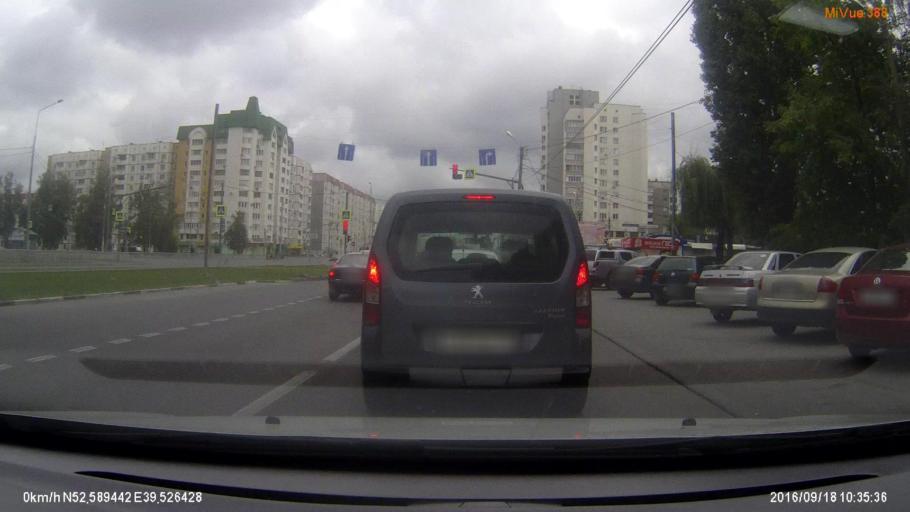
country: RU
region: Lipetsk
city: Syrskoye
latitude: 52.5855
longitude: 39.5306
